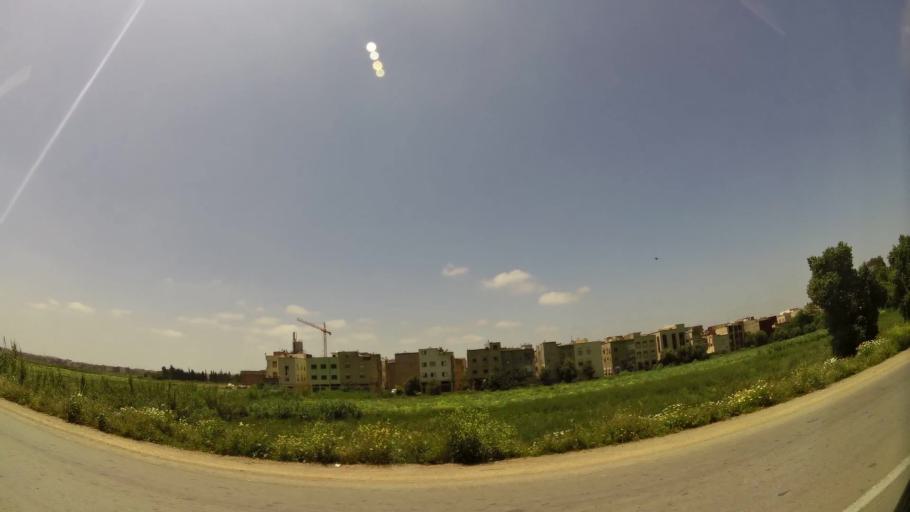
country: MA
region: Fes-Boulemane
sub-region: Fes
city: Fes
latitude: 34.0361
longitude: -5.0324
